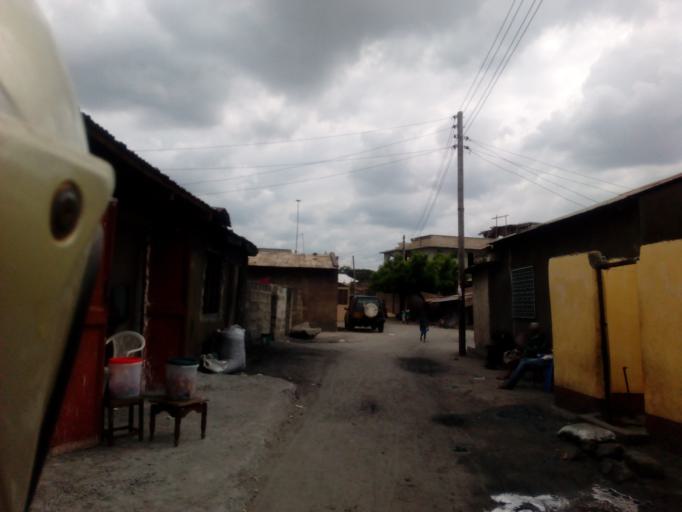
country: TZ
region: Dar es Salaam
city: Dar es Salaam
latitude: -6.8526
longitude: 39.2558
